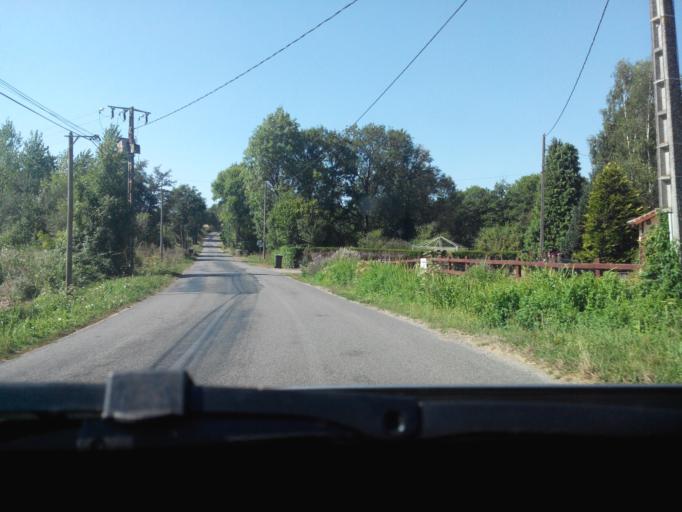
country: FR
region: Poitou-Charentes
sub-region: Departement de la Charente
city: Etagnac
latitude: 45.9441
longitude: 0.7770
